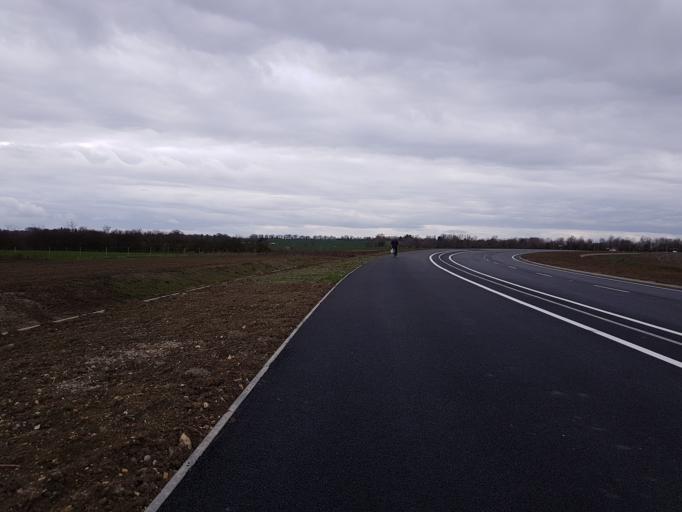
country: GB
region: England
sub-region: Cambridgeshire
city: Girton
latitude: 52.2408
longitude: 0.0454
